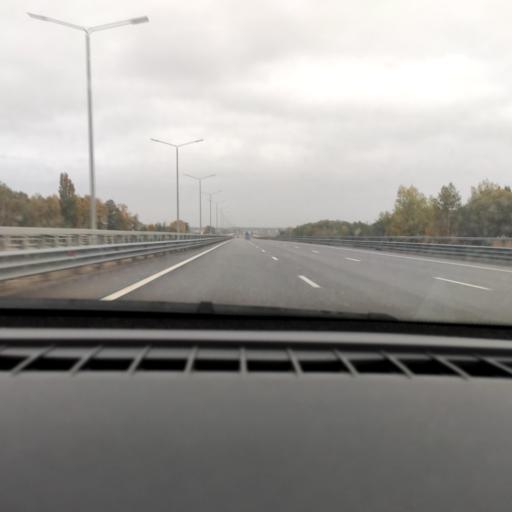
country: RU
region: Voronezj
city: Somovo
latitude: 51.7923
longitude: 39.2693
